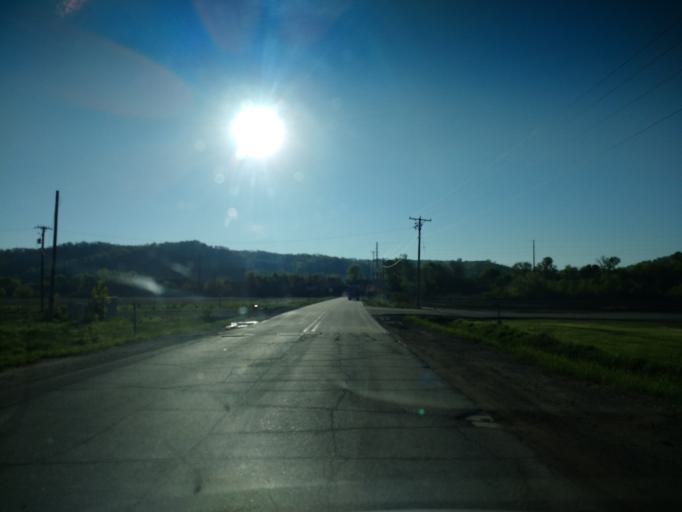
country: US
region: Iowa
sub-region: Harrison County
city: Missouri Valley
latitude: 41.4993
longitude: -95.8989
